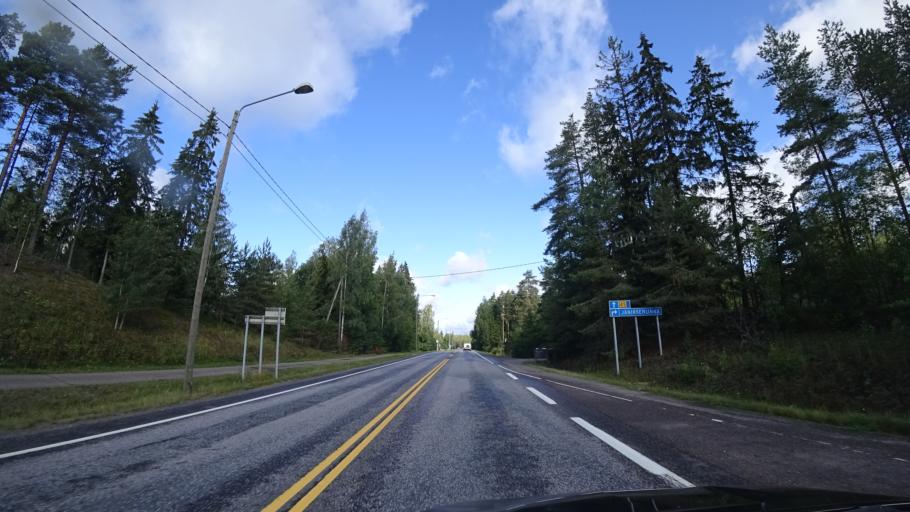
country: FI
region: Uusimaa
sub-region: Helsinki
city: Tuusula
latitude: 60.4399
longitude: 24.9786
